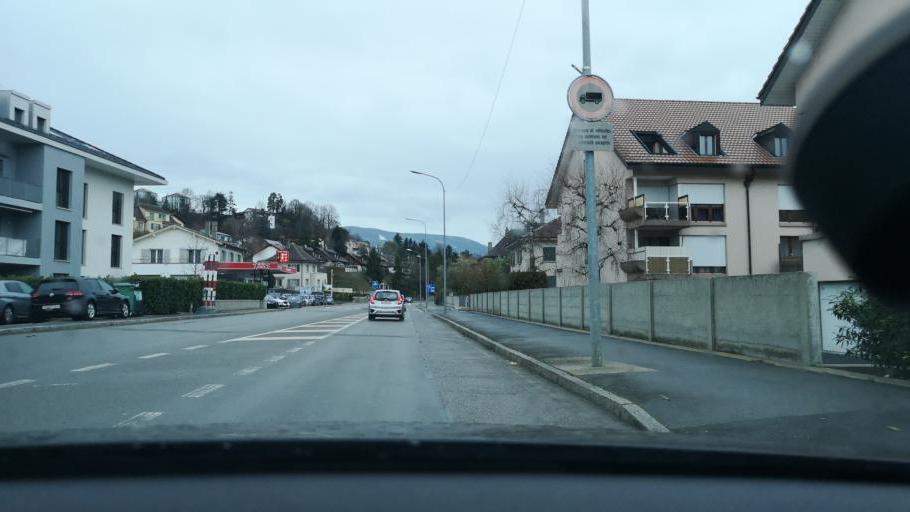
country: CH
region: Vaud
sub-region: Jura-Nord vaudois District
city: Montagny
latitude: 46.7993
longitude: 6.6287
